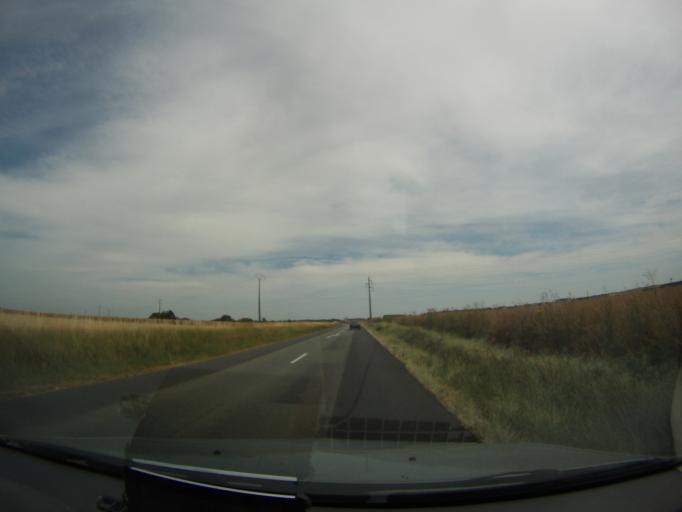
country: FR
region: Poitou-Charentes
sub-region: Departement de la Vienne
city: Mirebeau
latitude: 46.7749
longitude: 0.1402
